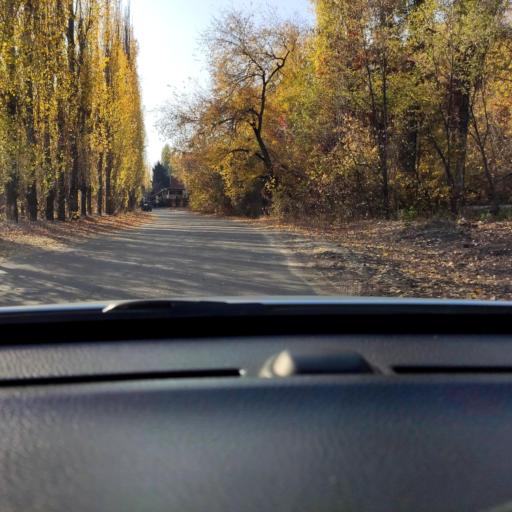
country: RU
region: Voronezj
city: Voronezh
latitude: 51.7020
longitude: 39.2366
